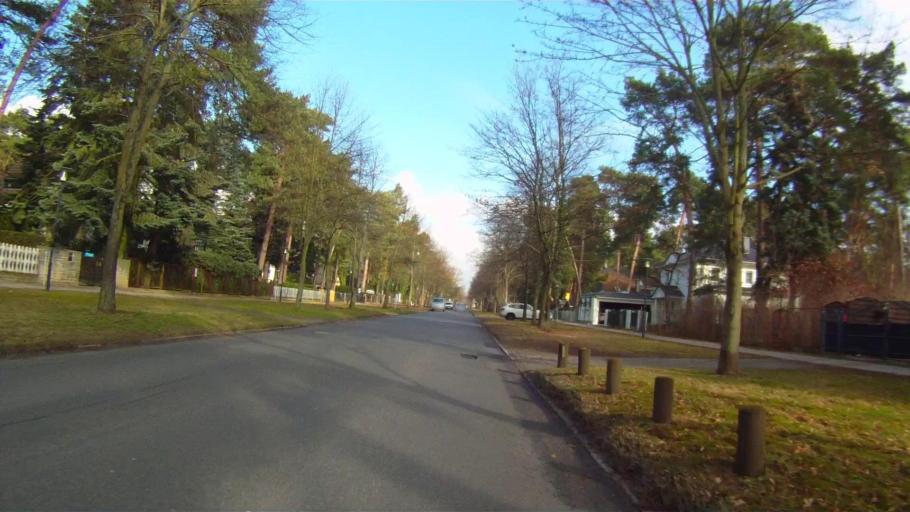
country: DE
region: Berlin
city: Friedrichshagen
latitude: 52.4791
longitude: 13.6221
